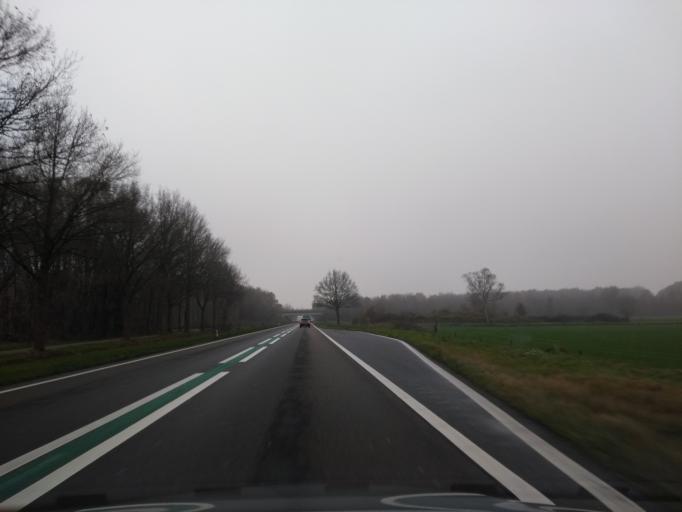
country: NL
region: Drenthe
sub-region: Gemeente Hoogeveen
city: Hoogeveen
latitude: 52.6470
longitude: 6.4368
